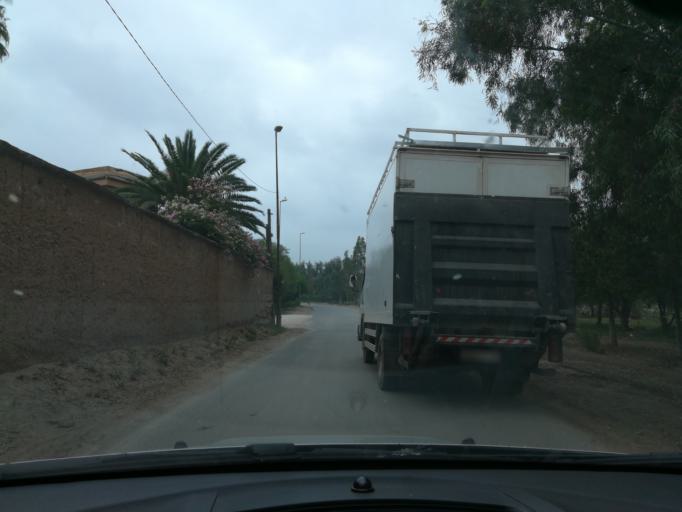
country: MA
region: Marrakech-Tensift-Al Haouz
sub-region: Marrakech
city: Marrakesh
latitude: 31.6584
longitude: -7.9834
